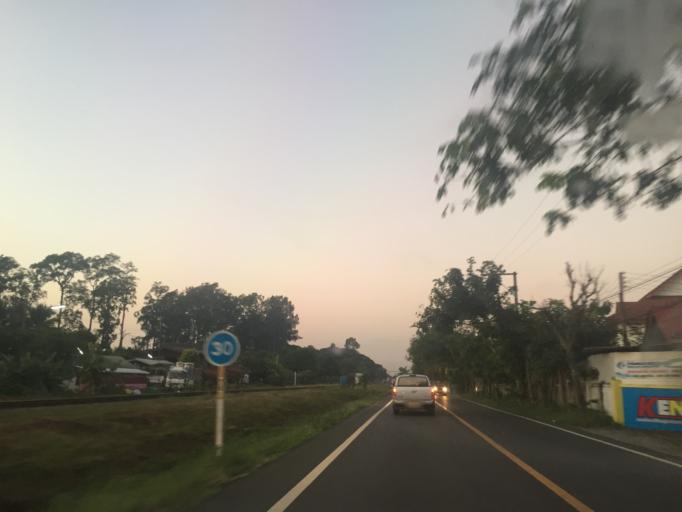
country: TH
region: Chiang Mai
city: Saraphi
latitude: 18.6904
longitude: 99.0453
